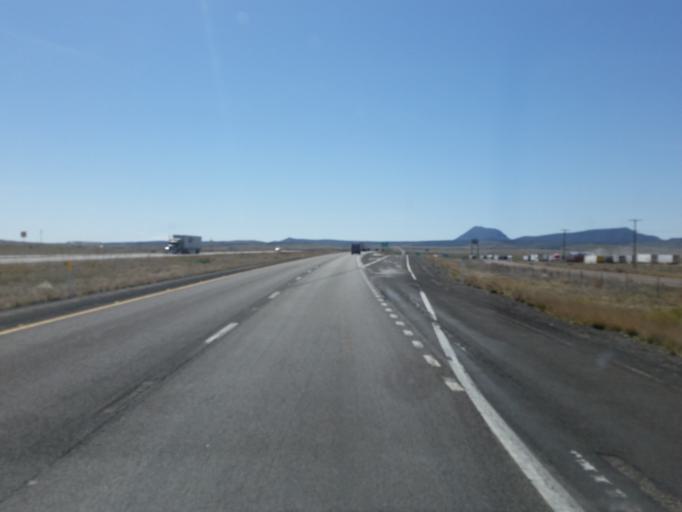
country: US
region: Arizona
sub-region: Yavapai County
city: Paulden
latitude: 35.3125
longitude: -112.8602
